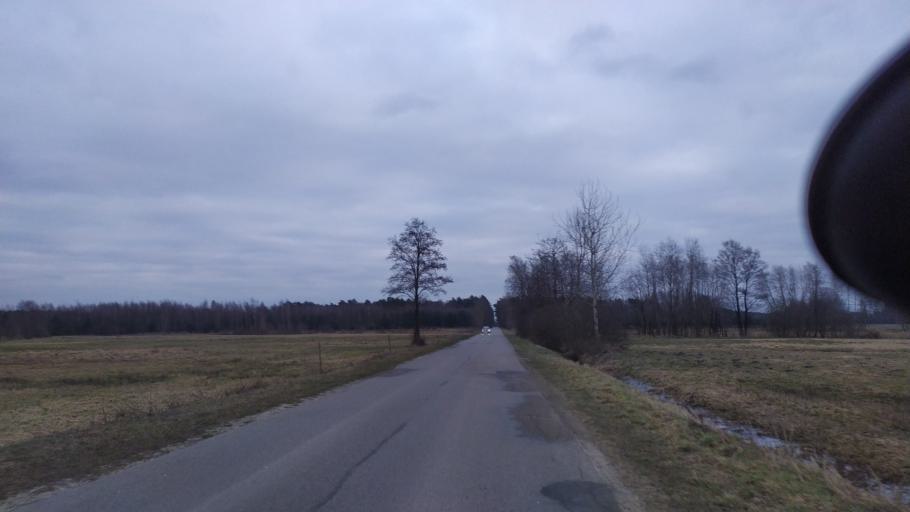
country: PL
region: Lublin Voivodeship
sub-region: Powiat lubartowski
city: Abramow
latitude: 51.4248
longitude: 22.3156
